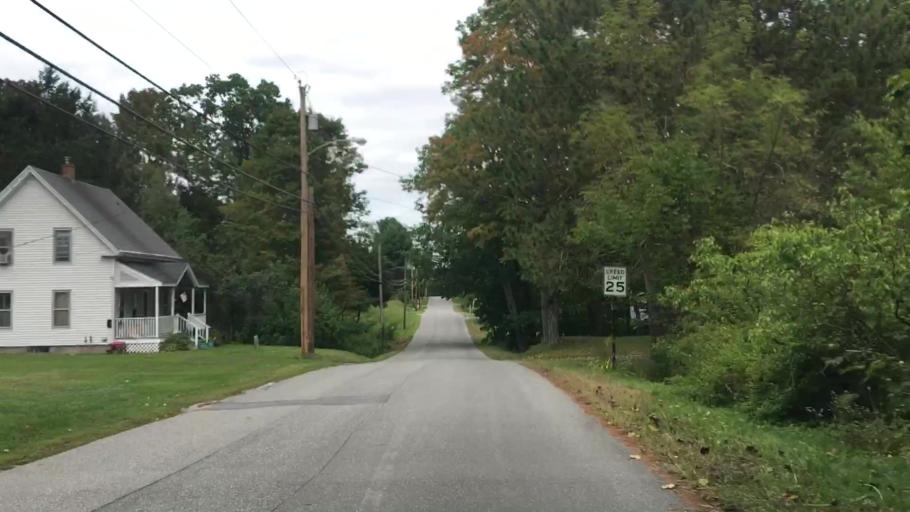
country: US
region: Maine
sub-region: Kennebec County
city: Hallowell
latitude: 44.2677
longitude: -69.7930
